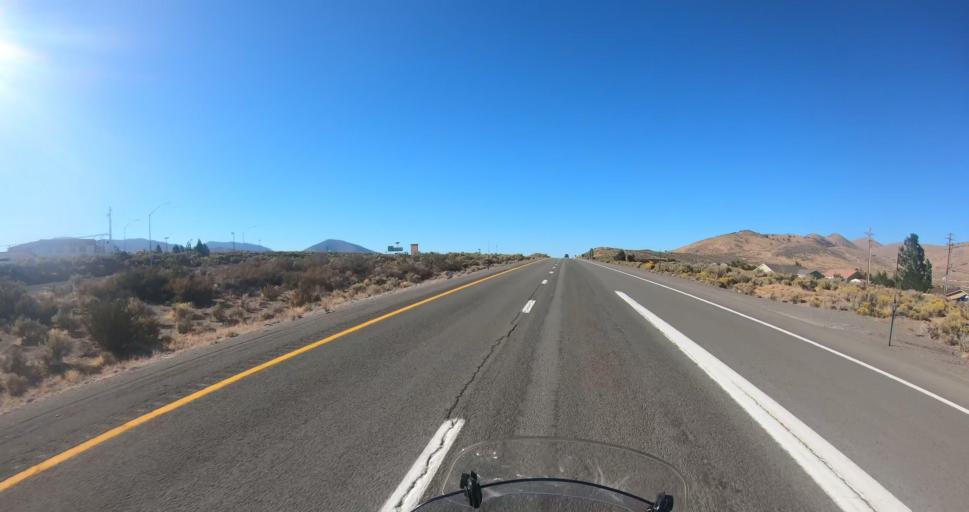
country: US
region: Nevada
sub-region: Washoe County
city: Cold Springs
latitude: 39.6711
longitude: -119.9987
